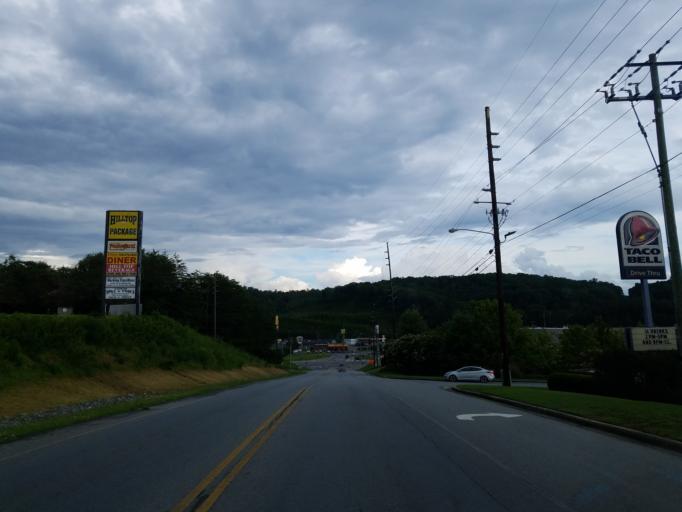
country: US
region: Georgia
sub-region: Gilmer County
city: Ellijay
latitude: 34.6786
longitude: -84.4811
